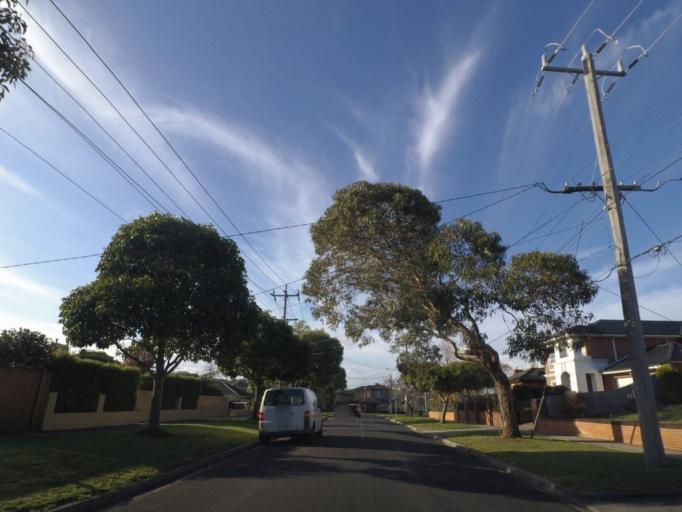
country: AU
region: Victoria
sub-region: Whitehorse
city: Box Hill North
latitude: -37.7999
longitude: 145.1343
